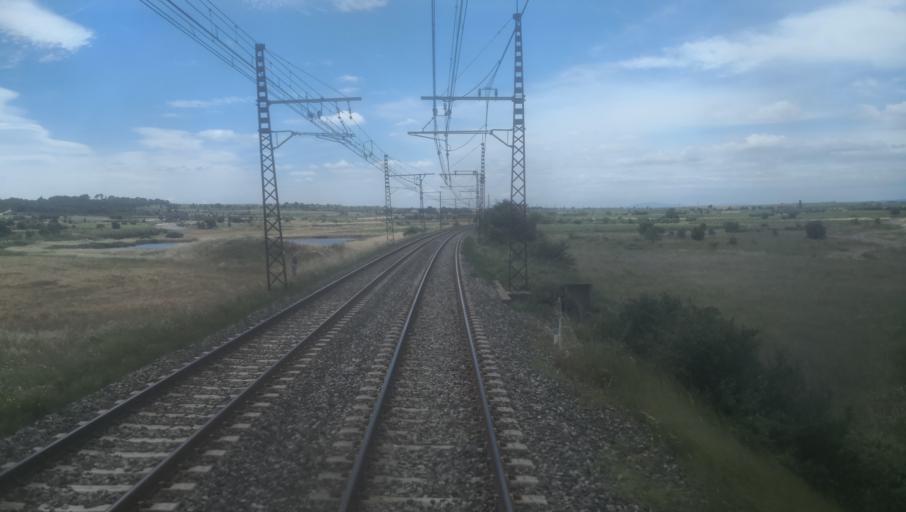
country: FR
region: Languedoc-Roussillon
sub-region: Departement de l'Herault
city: Nissan-lez-Enserune
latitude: 43.2880
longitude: 3.1081
